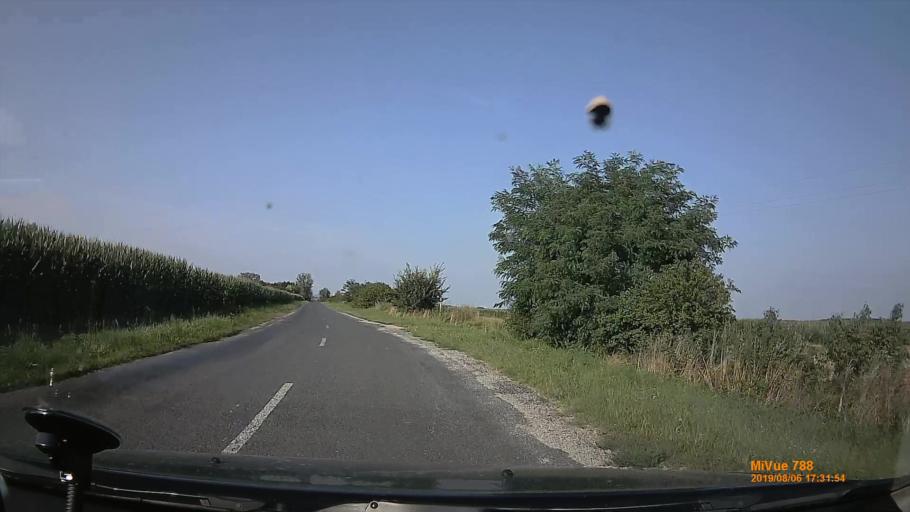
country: HU
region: Zala
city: Murakeresztur
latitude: 46.4162
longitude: 16.8744
